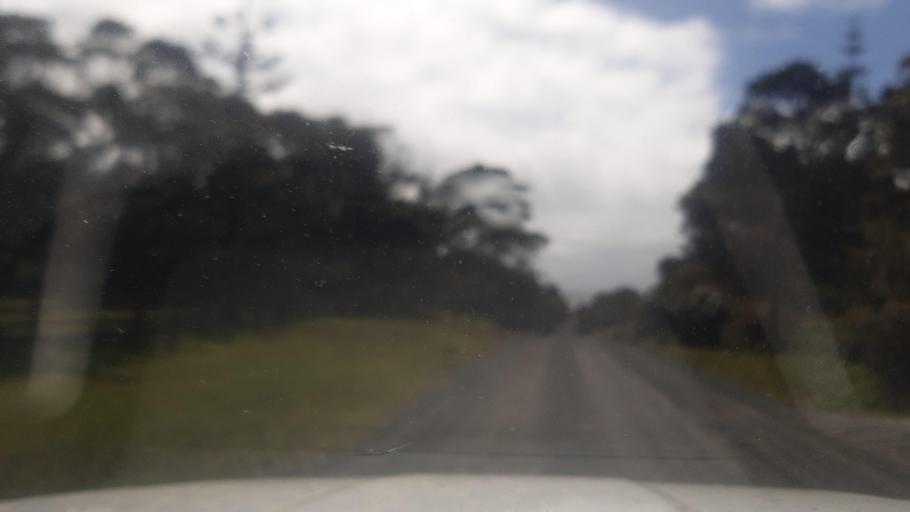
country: NZ
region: Northland
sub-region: Far North District
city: Kaitaia
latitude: -34.7438
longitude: 173.1043
